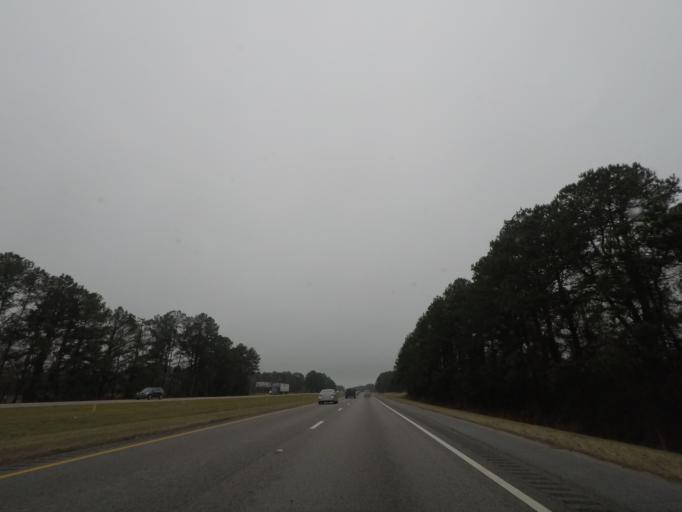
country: US
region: South Carolina
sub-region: Florence County
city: Timmonsville
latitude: 33.9548
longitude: -80.0506
